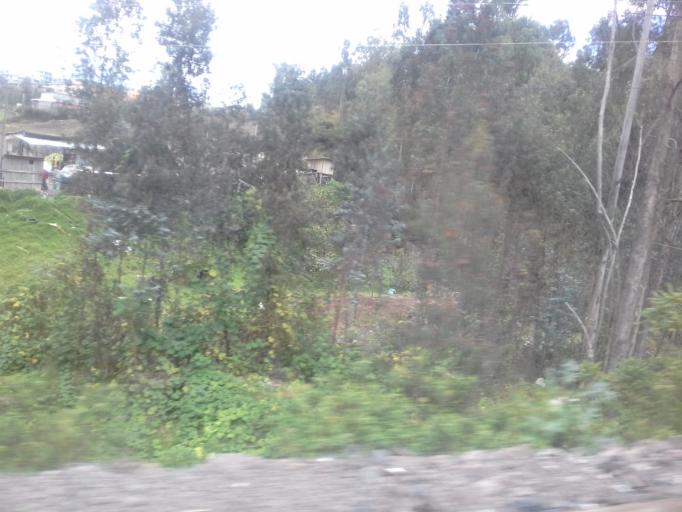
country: EC
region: Pichincha
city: Sangolqui
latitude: -0.3305
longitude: -78.4182
